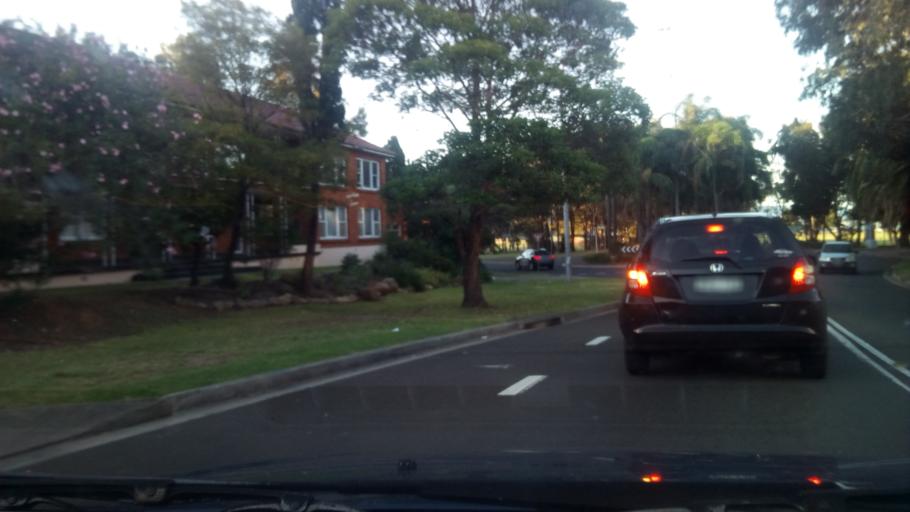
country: AU
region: New South Wales
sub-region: Wollongong
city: Wollongong
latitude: -34.4134
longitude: 150.8998
